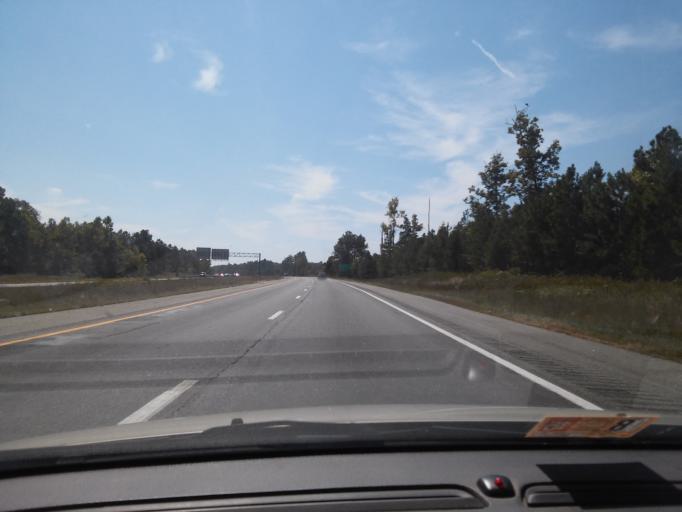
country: US
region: Virginia
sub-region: Henrico County
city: Short Pump
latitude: 37.6498
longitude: -77.6655
